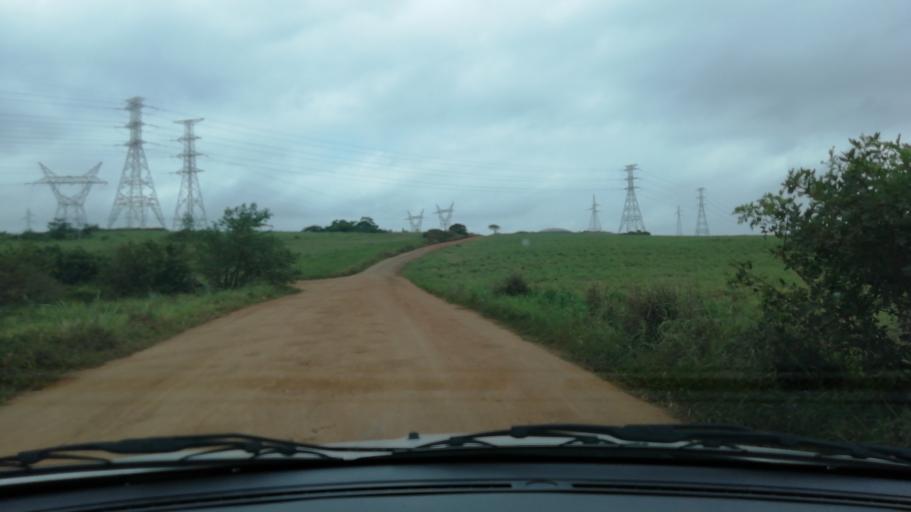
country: ZA
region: KwaZulu-Natal
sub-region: uThungulu District Municipality
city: Empangeni
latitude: -28.7333
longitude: 31.8994
